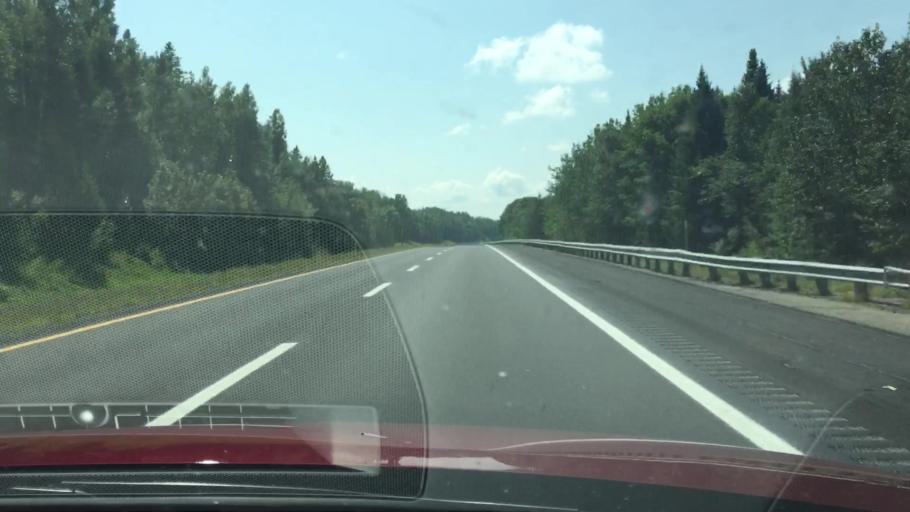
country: US
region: Maine
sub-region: Penobscot County
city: Patten
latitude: 45.9111
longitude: -68.3794
